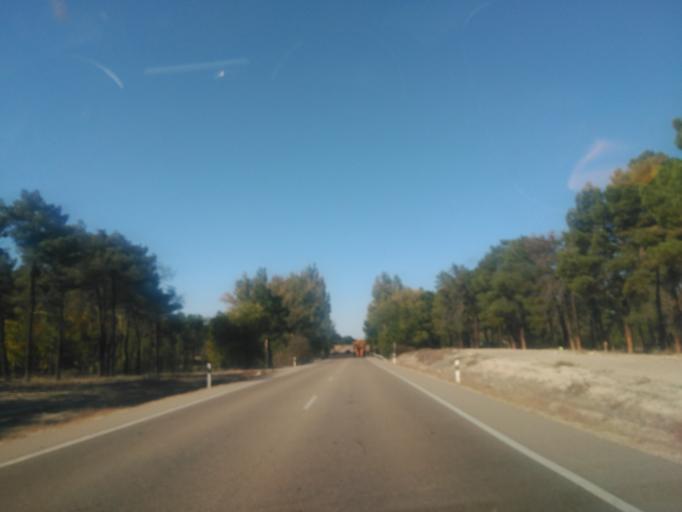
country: ES
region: Castille and Leon
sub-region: Provincia de Valladolid
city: Traspinedo
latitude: 41.6028
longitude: -4.4656
